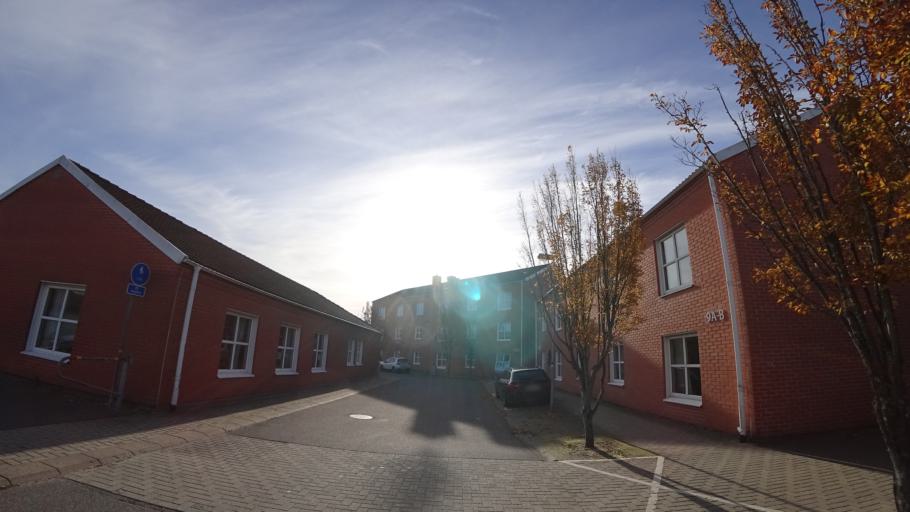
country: SE
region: Skane
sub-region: Staffanstorps Kommun
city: Staffanstorp
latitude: 55.6381
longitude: 13.2188
